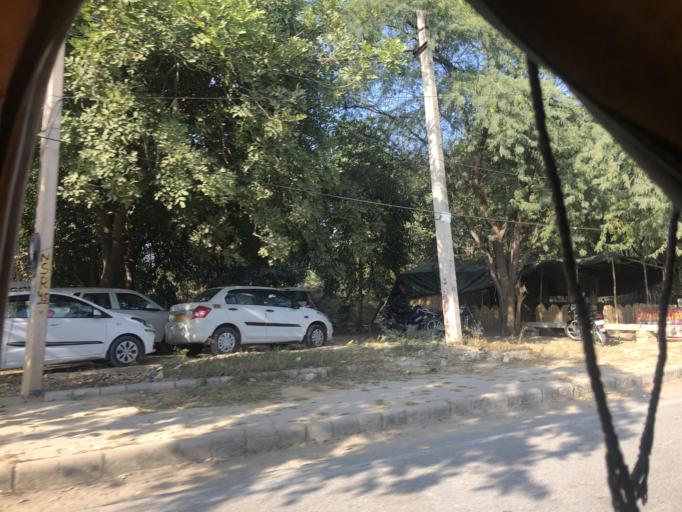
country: IN
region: Haryana
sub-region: Gurgaon
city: Gurgaon
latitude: 28.4642
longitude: 77.0714
